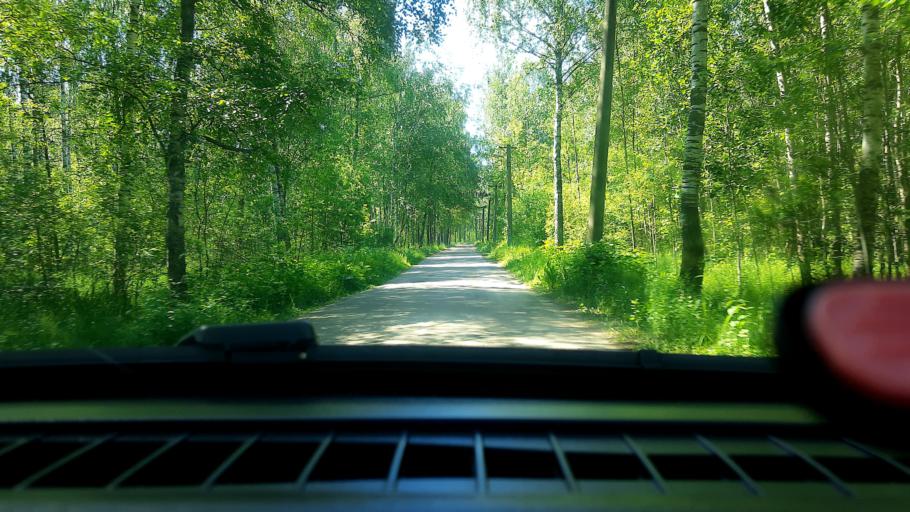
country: RU
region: Nizjnij Novgorod
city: Gorbatovka
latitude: 56.2864
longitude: 43.8299
